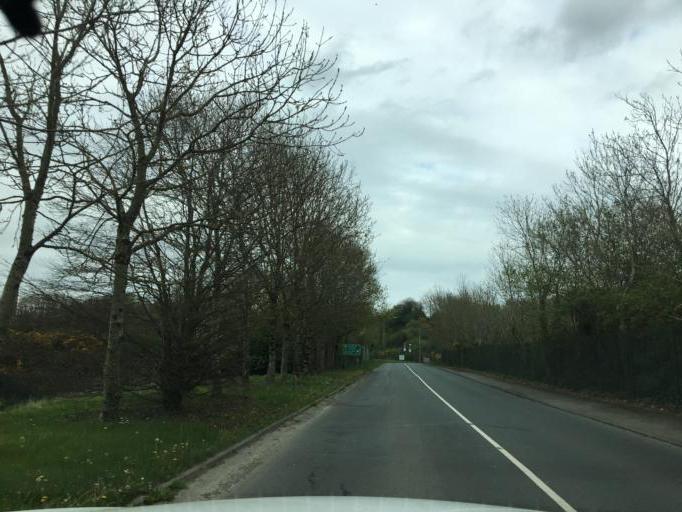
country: IE
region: Leinster
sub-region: Loch Garman
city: Loch Garman
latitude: 52.3485
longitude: -6.5162
